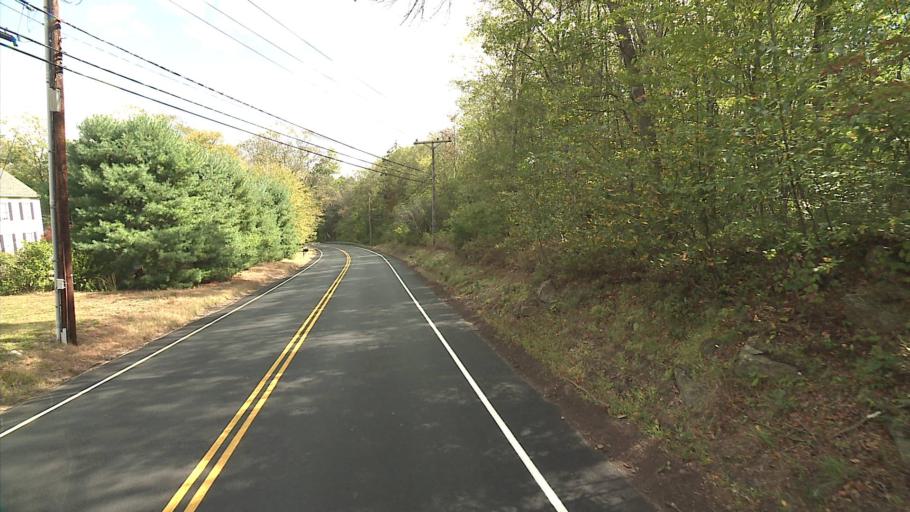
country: US
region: Connecticut
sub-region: Middlesex County
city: Chester Center
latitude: 41.3900
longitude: -72.5566
